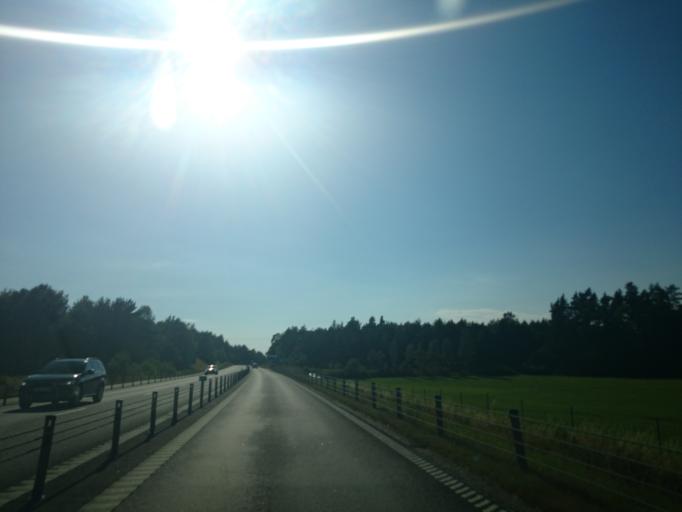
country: SE
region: Blekinge
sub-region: Ronneby Kommun
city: Kallinge
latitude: 56.1997
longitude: 15.3872
